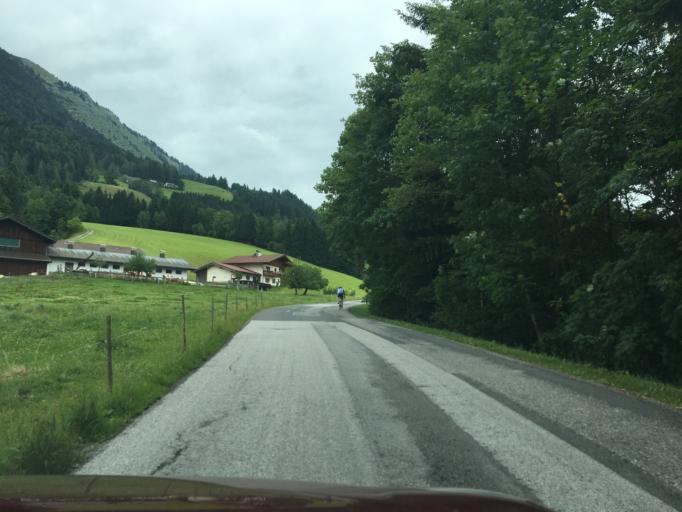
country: AT
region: Salzburg
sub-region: Politischer Bezirk Hallein
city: Abtenau
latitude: 47.5998
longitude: 13.3457
